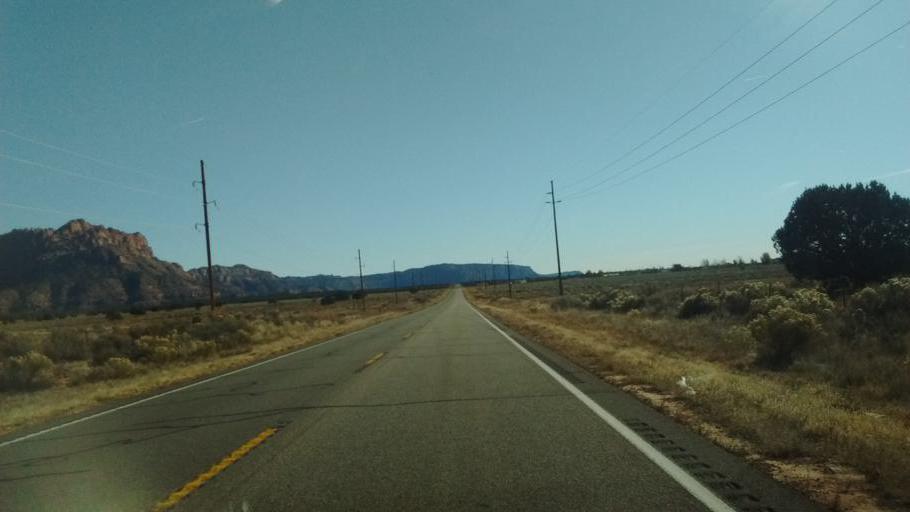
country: US
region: Arizona
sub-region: Mohave County
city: Colorado City
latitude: 37.0332
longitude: -113.0617
